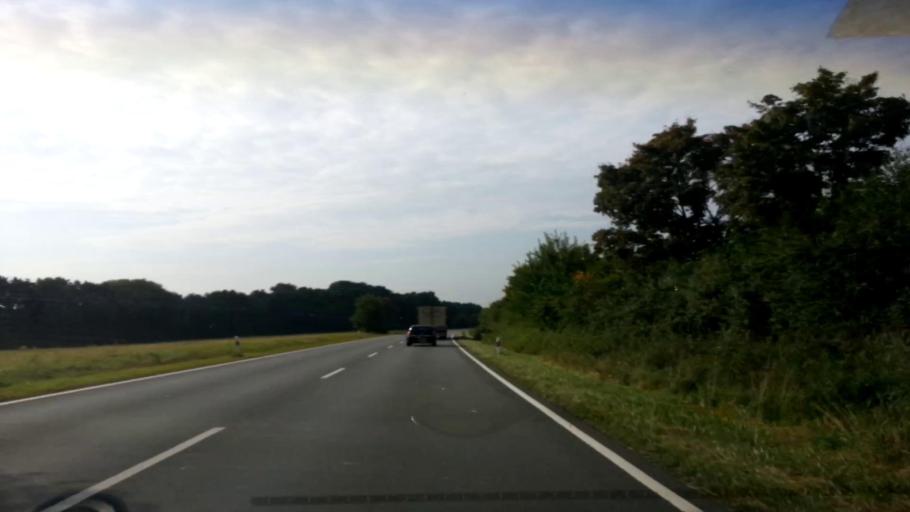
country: DE
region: Bavaria
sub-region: Regierungsbezirk Unterfranken
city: Prichsenstadt
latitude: 49.8058
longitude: 10.3608
